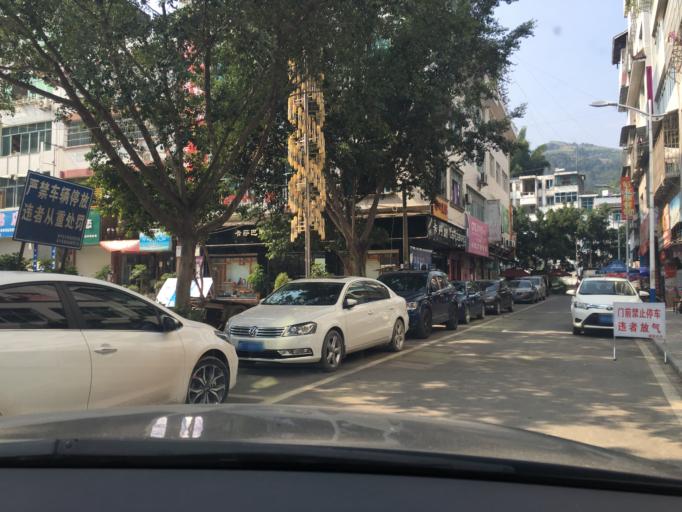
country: CN
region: Guangxi Zhuangzu Zizhiqu
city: Xinzhou
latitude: 24.9860
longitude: 105.8060
